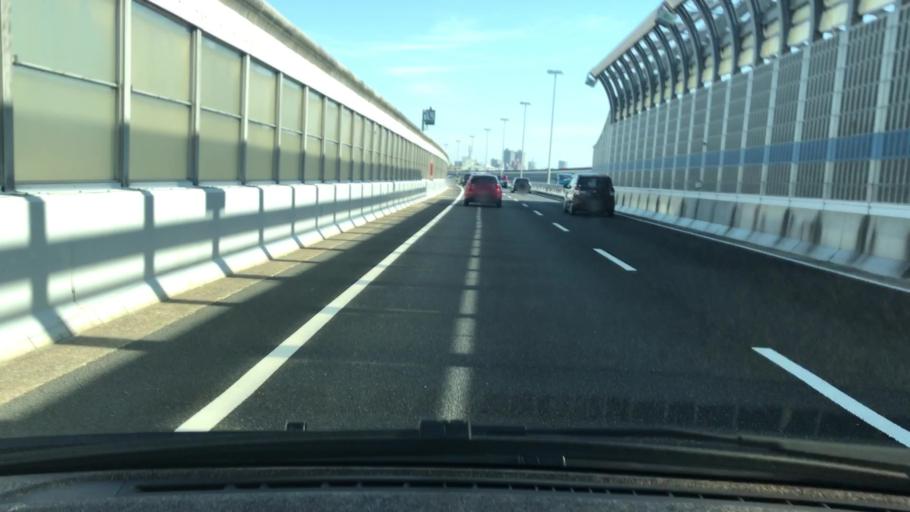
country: JP
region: Hyogo
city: Ashiya
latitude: 34.7274
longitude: 135.3089
